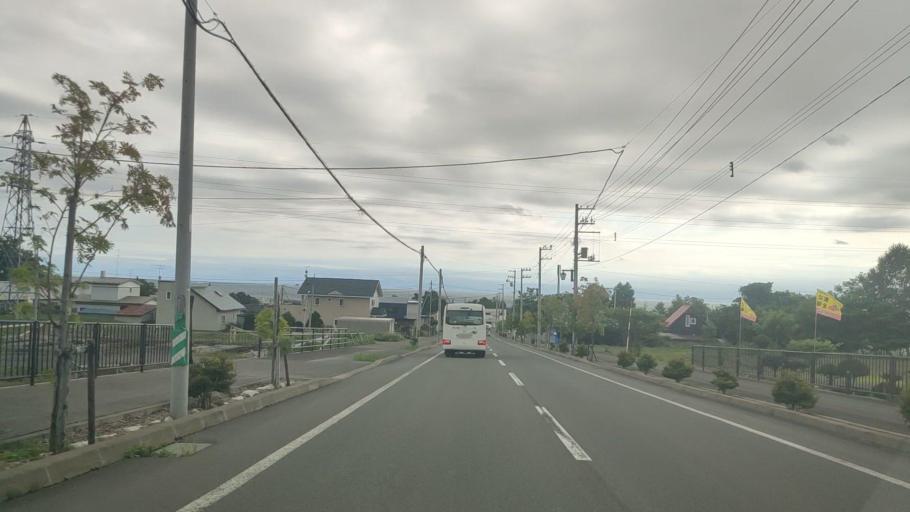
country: JP
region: Hokkaido
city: Date
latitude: 42.5527
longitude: 140.7711
